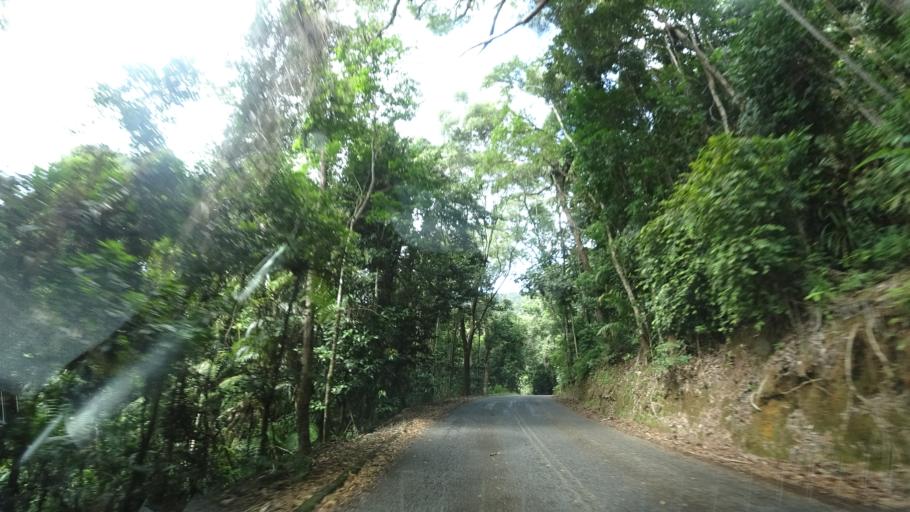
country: AU
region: Queensland
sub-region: Cairns
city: Port Douglas
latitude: -16.2388
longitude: 145.4268
